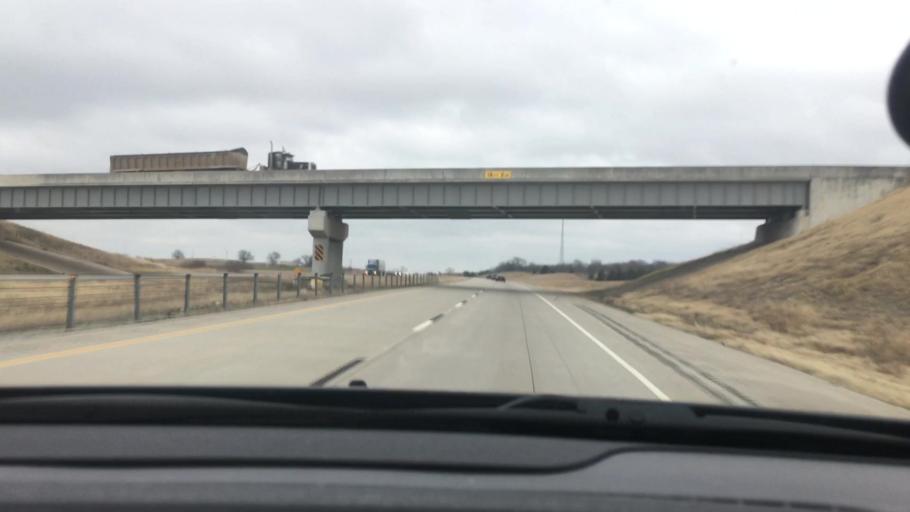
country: US
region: Oklahoma
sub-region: Bryan County
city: Durant
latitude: 34.1315
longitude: -96.2745
